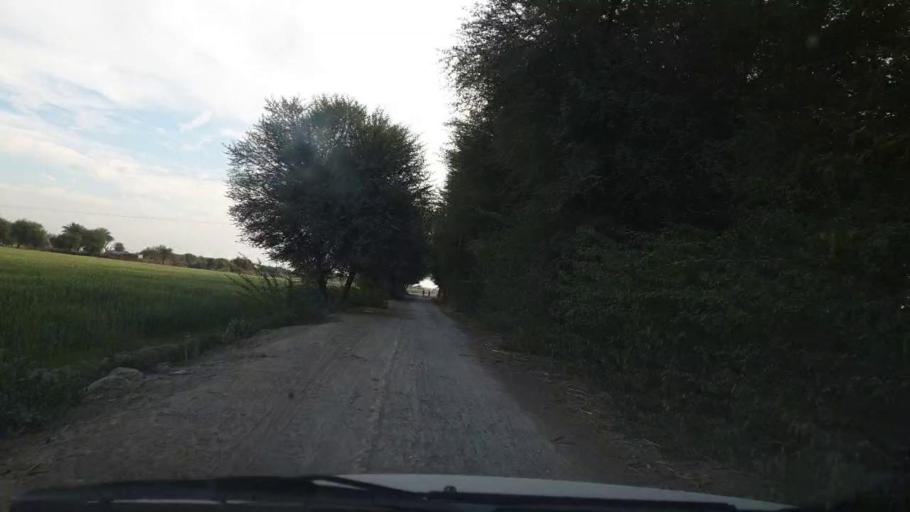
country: PK
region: Sindh
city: Pithoro
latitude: 25.6452
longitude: 69.2761
